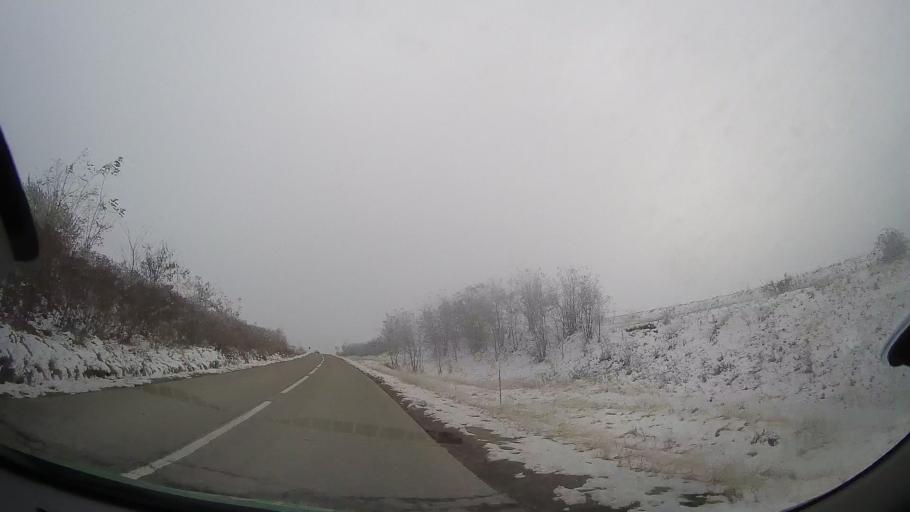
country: RO
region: Vaslui
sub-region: Comuna Ivesti
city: Ivesti
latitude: 46.2064
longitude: 27.5059
